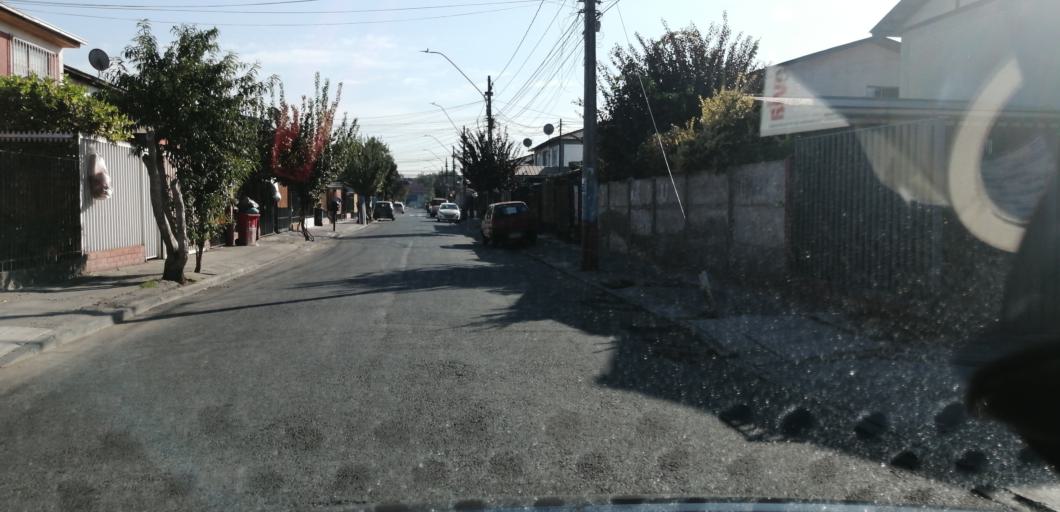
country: CL
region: Santiago Metropolitan
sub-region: Provincia de Santiago
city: Lo Prado
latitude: -33.4590
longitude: -70.7447
